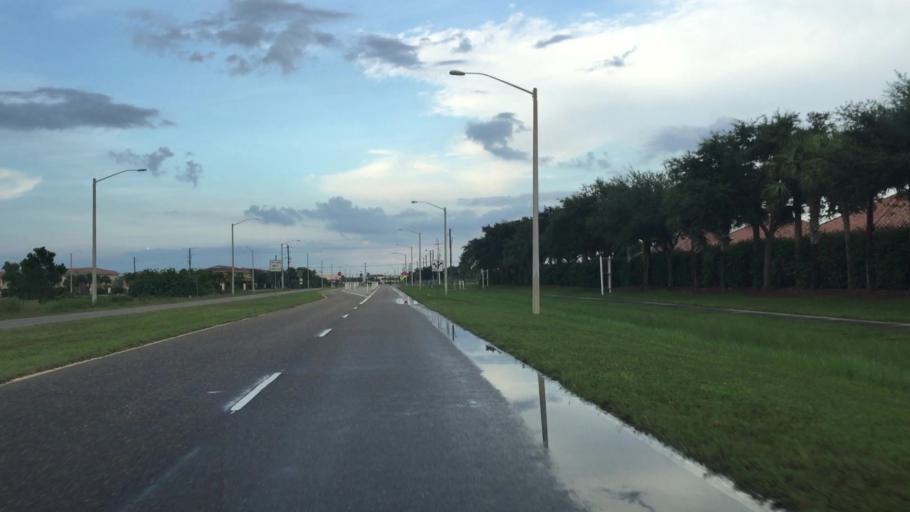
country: US
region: Florida
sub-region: Lee County
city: Fort Myers
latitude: 26.6025
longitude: -81.8206
